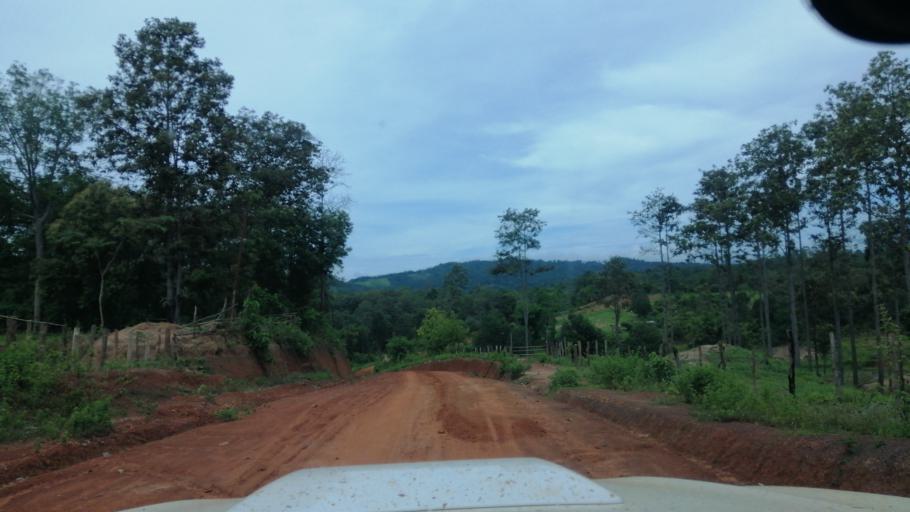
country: TH
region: Loei
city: Na Haeo
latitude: 17.5781
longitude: 101.1558
